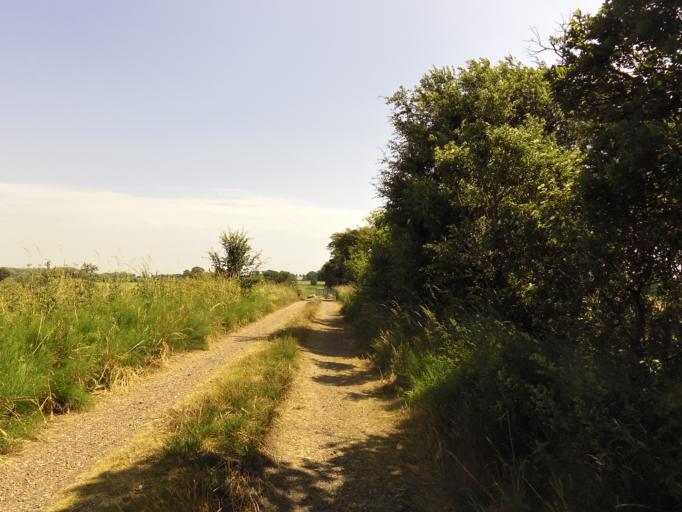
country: DK
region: South Denmark
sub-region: Haderslev Kommune
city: Vojens
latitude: 55.1584
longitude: 9.2395
